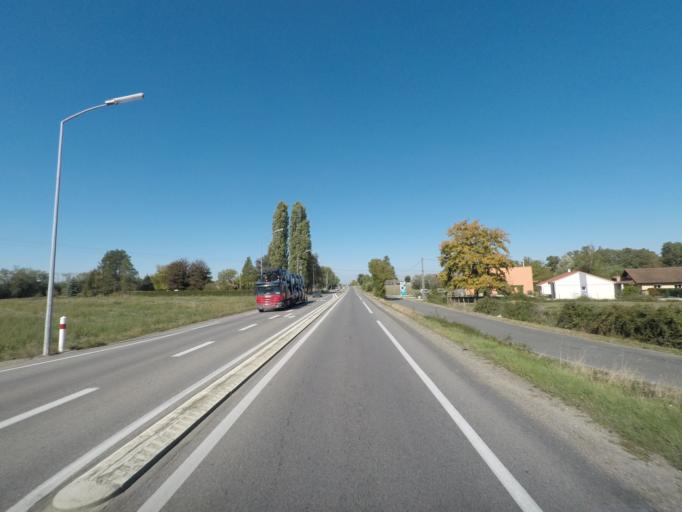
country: FR
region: Rhone-Alpes
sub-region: Departement de l'Ain
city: Viriat
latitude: 46.2489
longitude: 5.1859
